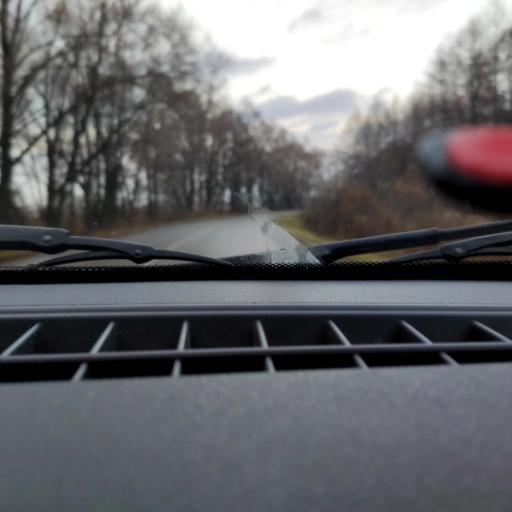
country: RU
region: Bashkortostan
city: Avdon
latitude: 54.5109
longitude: 55.8645
